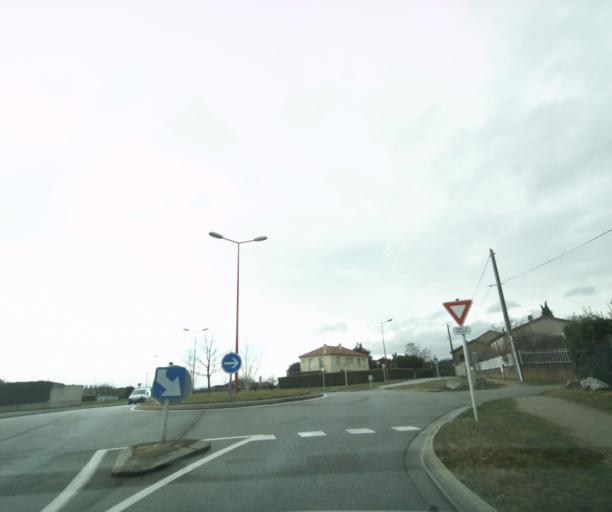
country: FR
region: Rhone-Alpes
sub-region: Departement de la Drome
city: Bourg-les-Valence
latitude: 44.9578
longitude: 4.9141
